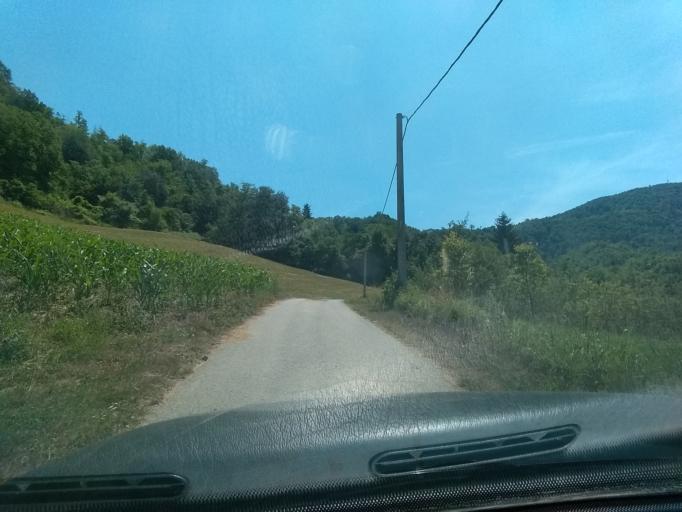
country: SI
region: Bistrica ob Sotli
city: Bistrica ob Sotli
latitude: 46.0700
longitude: 15.7458
